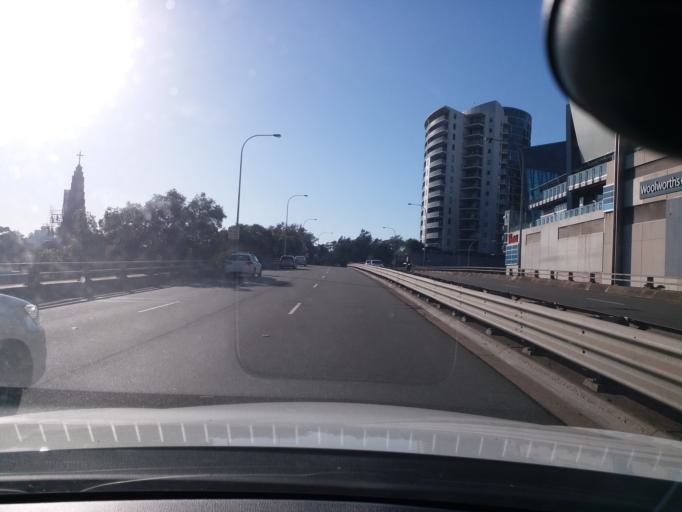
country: AU
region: New South Wales
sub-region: Waverley
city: Bondi Junction
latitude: -33.8907
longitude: 151.2503
